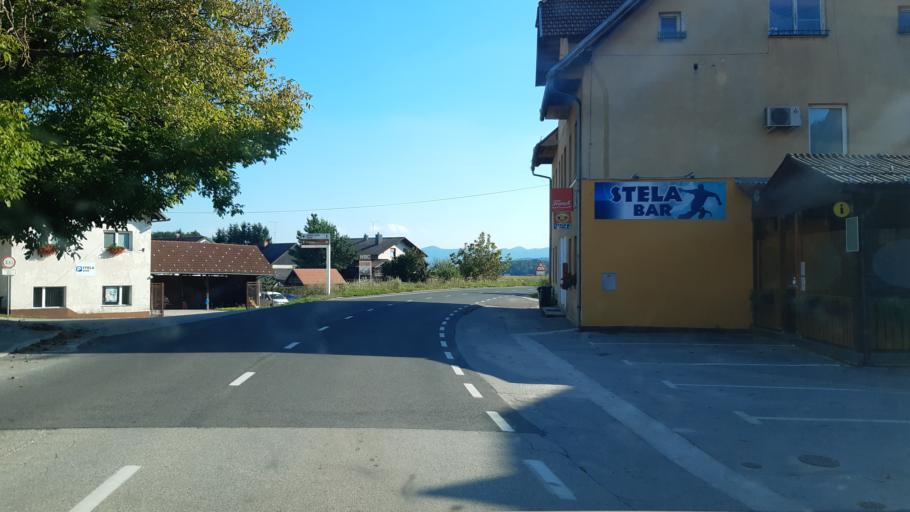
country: SI
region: Ivancna Gorica
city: Ivancna Gorica
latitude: 45.9551
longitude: 14.8065
